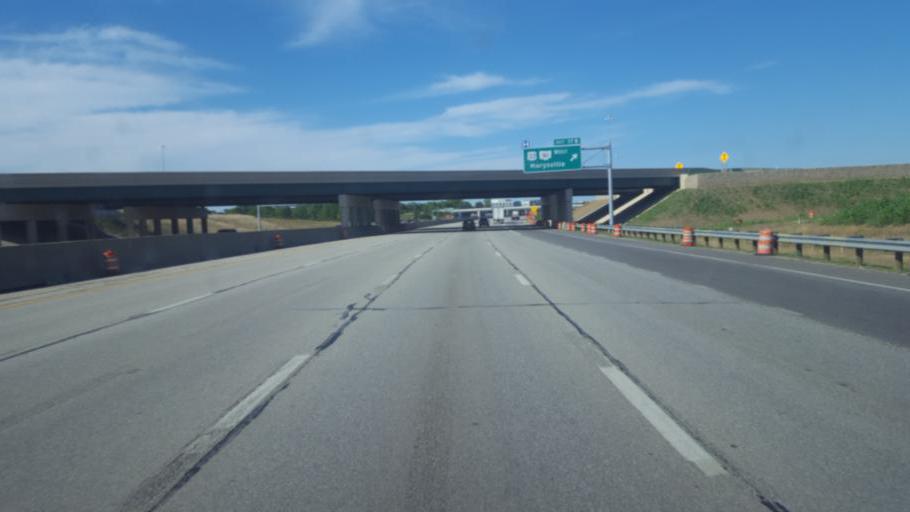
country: US
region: Ohio
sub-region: Franklin County
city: Dublin
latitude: 40.0981
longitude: -83.1350
